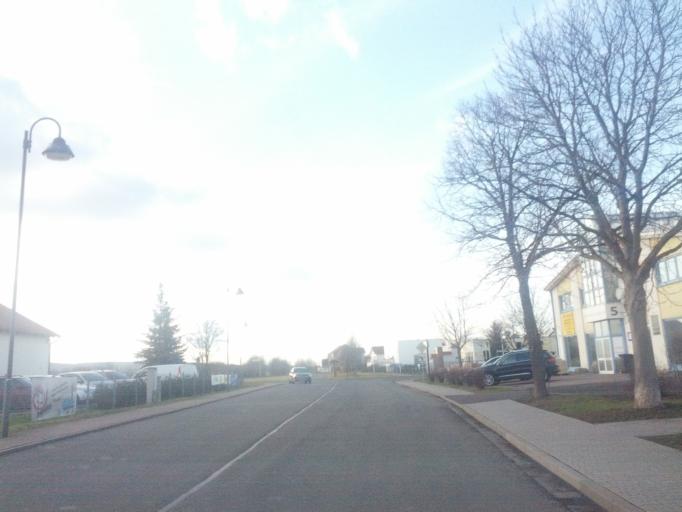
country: DE
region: Thuringia
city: Apfelstadt
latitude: 50.9004
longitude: 10.8808
